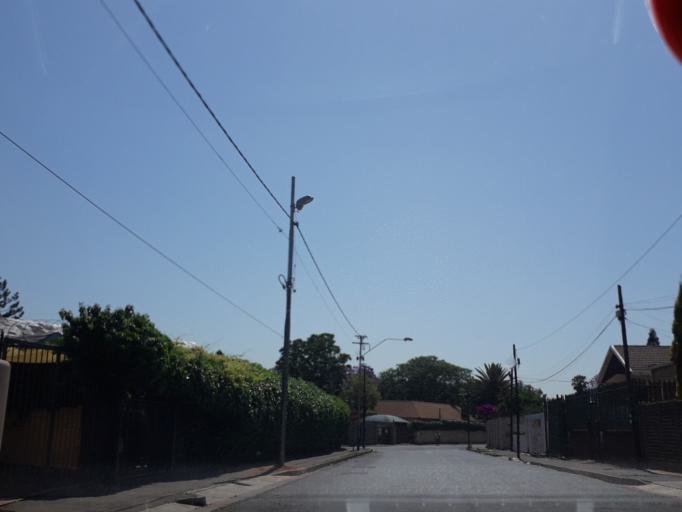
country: ZA
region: Gauteng
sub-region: City of Johannesburg Metropolitan Municipality
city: Johannesburg
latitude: -26.1644
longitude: 28.0849
